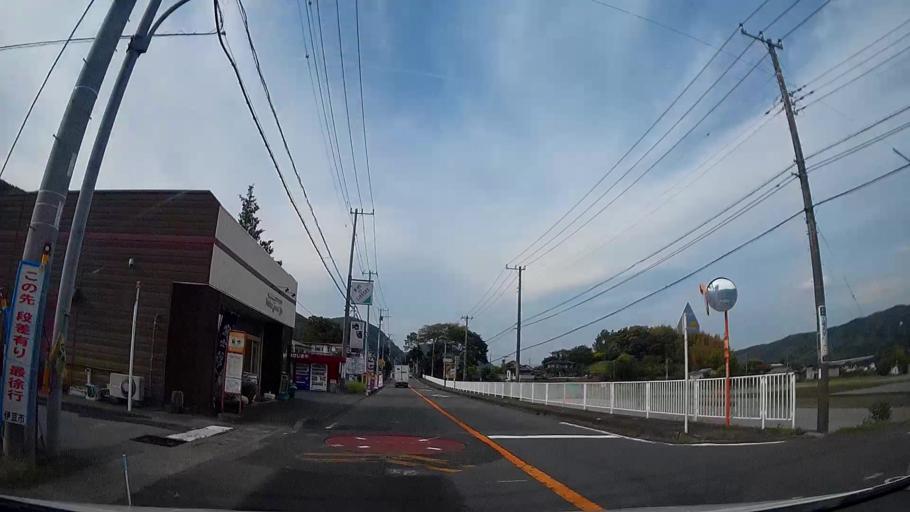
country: JP
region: Shizuoka
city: Ito
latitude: 34.9533
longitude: 138.9359
